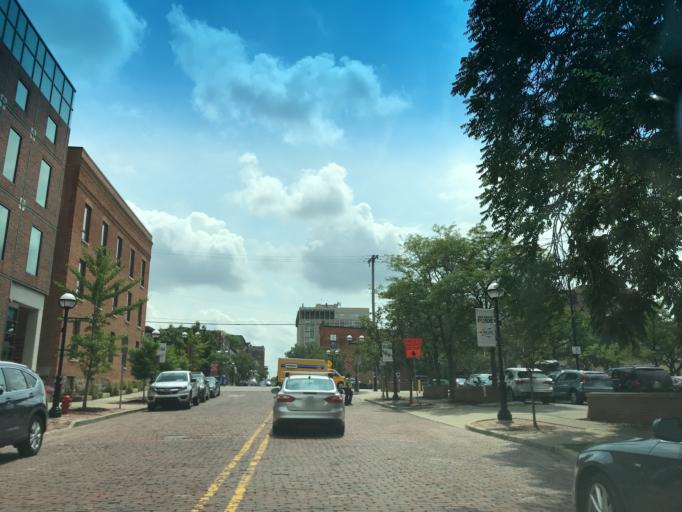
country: US
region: Michigan
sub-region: Washtenaw County
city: Ann Arbor
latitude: 42.2839
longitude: -83.7472
